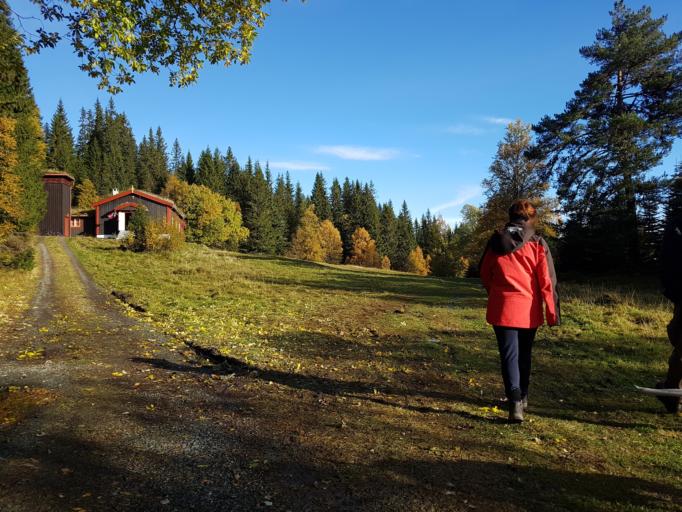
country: NO
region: Sor-Trondelag
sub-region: Trondheim
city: Trondheim
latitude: 63.4162
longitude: 10.2763
